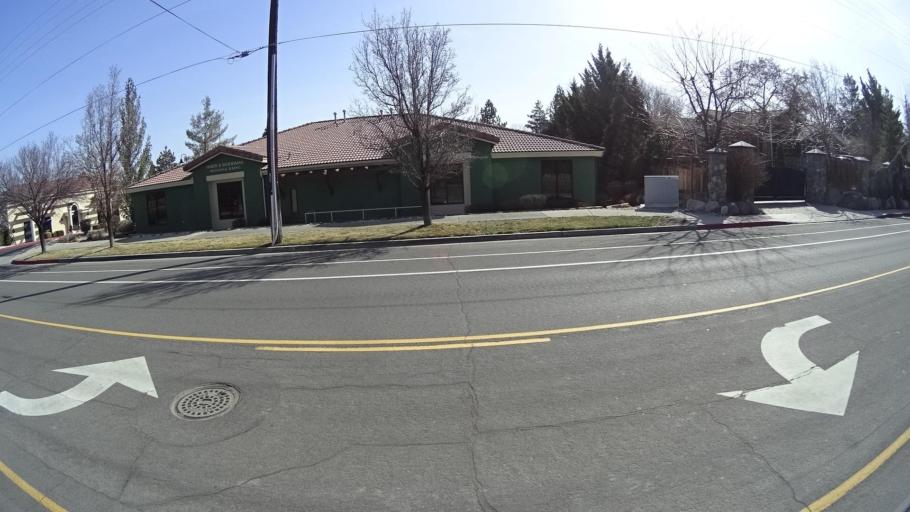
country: US
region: Nevada
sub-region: Washoe County
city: Reno
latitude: 39.5045
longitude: -119.8172
